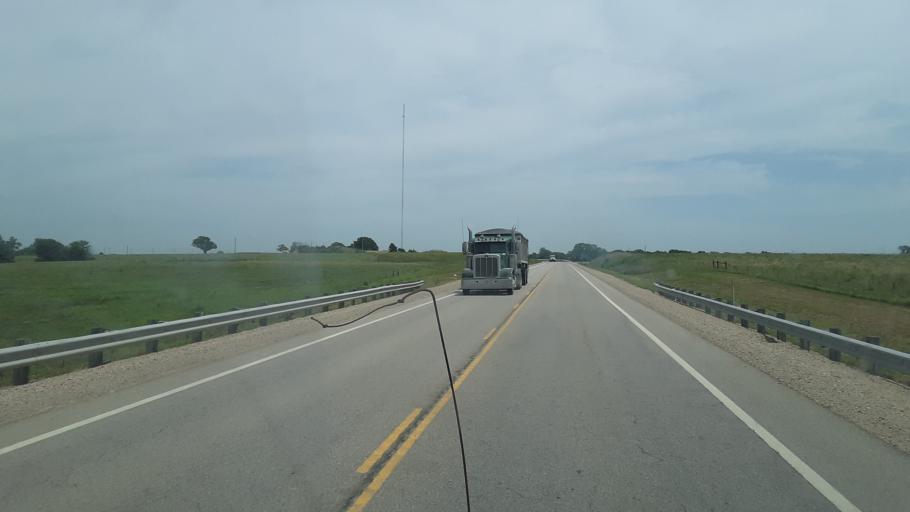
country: US
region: Kansas
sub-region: Greenwood County
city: Eureka
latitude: 37.8175
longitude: -96.2396
